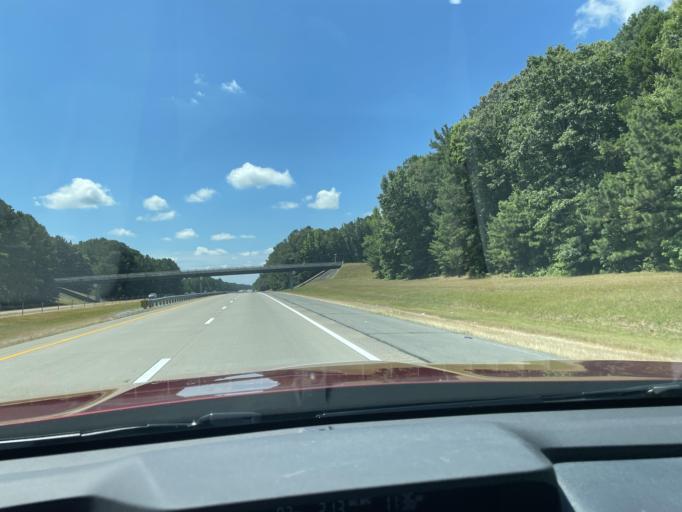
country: US
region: Arkansas
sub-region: Jefferson County
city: Redfield
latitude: 34.4412
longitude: -92.1975
